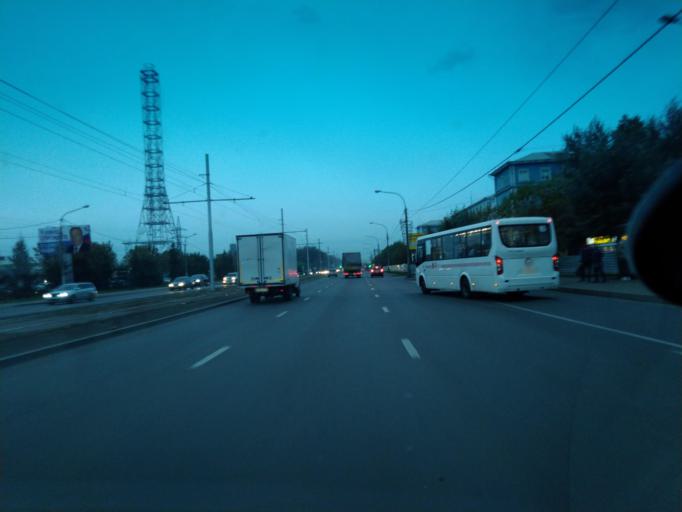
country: RU
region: Krasnoyarskiy
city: Berezovka
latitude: 56.0220
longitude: 93.0106
